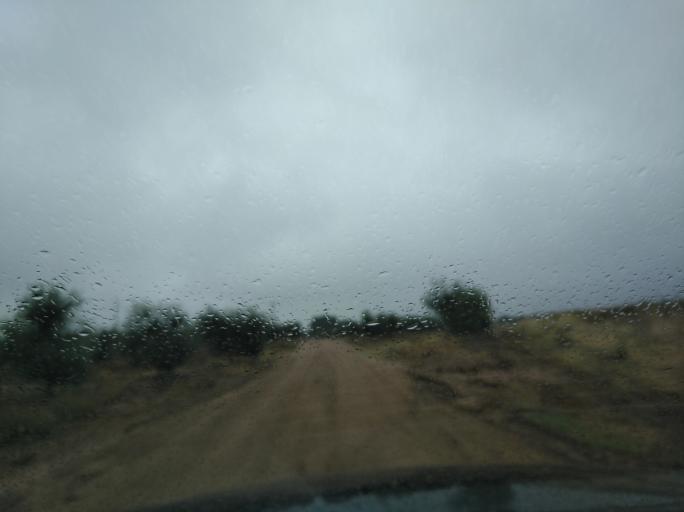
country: PT
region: Portalegre
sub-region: Campo Maior
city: Campo Maior
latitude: 38.9541
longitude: -7.0546
